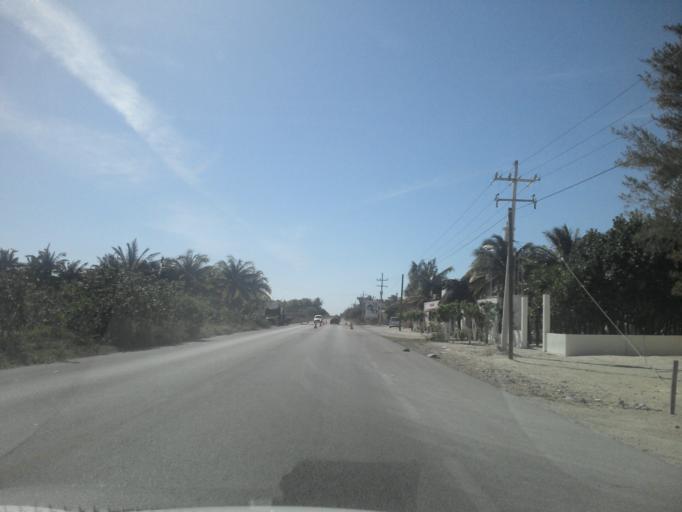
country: MX
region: Yucatan
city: Telchac Puerto
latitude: 21.3276
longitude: -89.4034
